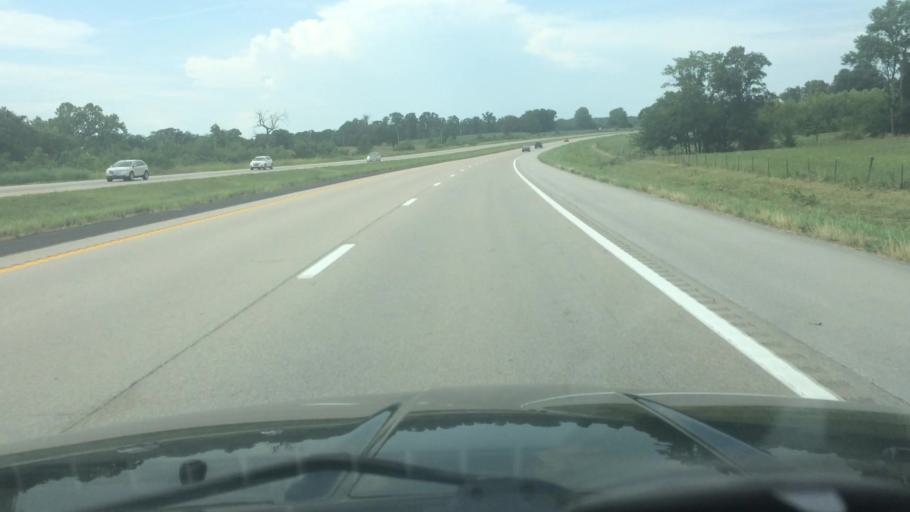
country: US
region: Missouri
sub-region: Polk County
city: Humansville
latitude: 37.8205
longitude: -93.6141
